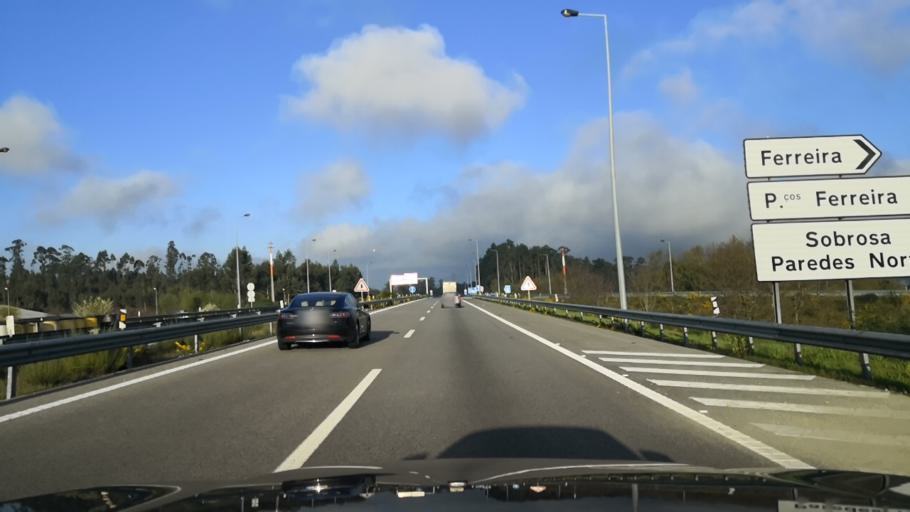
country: PT
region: Porto
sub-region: Pacos de Ferreira
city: Ferreira
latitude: 41.2587
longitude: -8.3633
